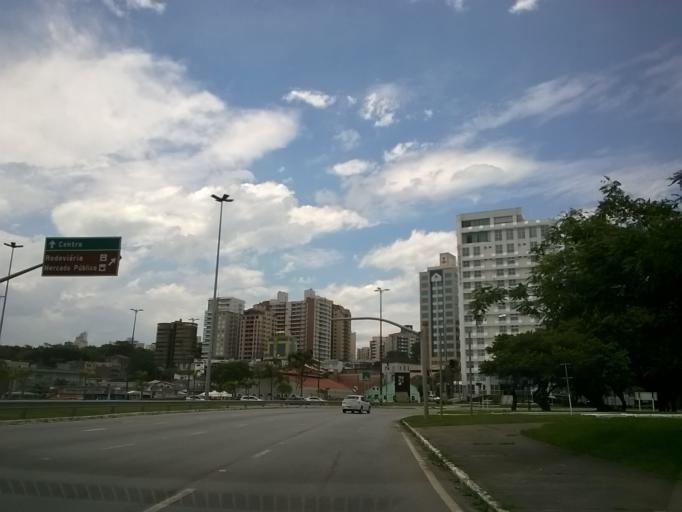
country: BR
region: Santa Catarina
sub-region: Florianopolis
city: Florianopolis
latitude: -27.5968
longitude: -48.5595
